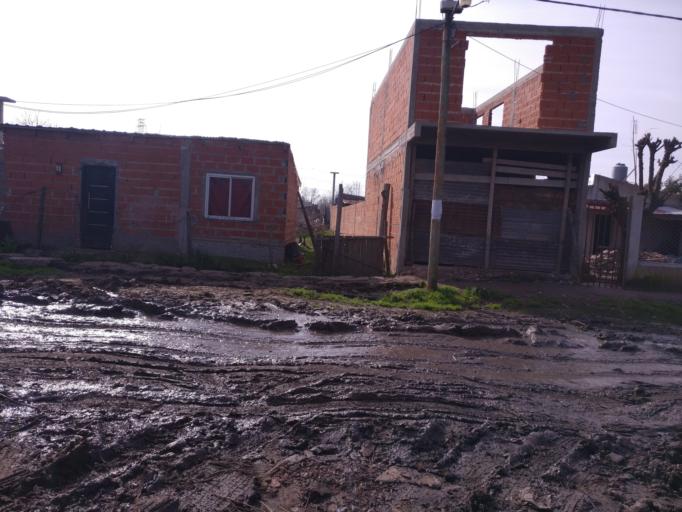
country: AR
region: Buenos Aires
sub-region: Partido de Ezeiza
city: Ezeiza
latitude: -34.9311
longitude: -58.6178
